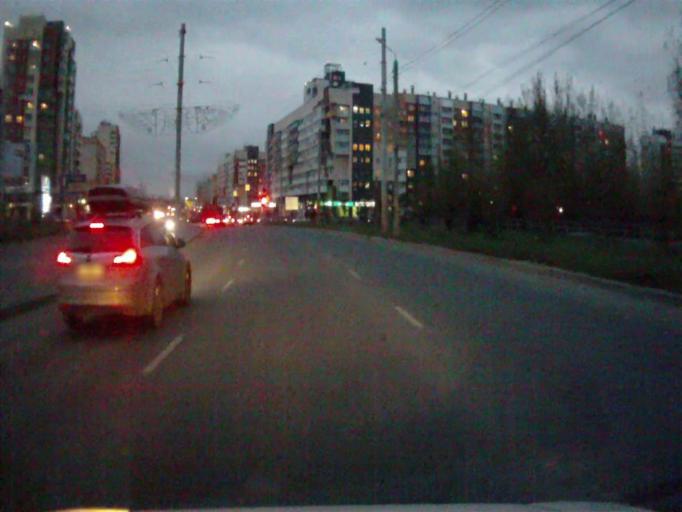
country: RU
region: Chelyabinsk
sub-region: Gorod Chelyabinsk
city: Chelyabinsk
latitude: 55.1681
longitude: 61.2950
